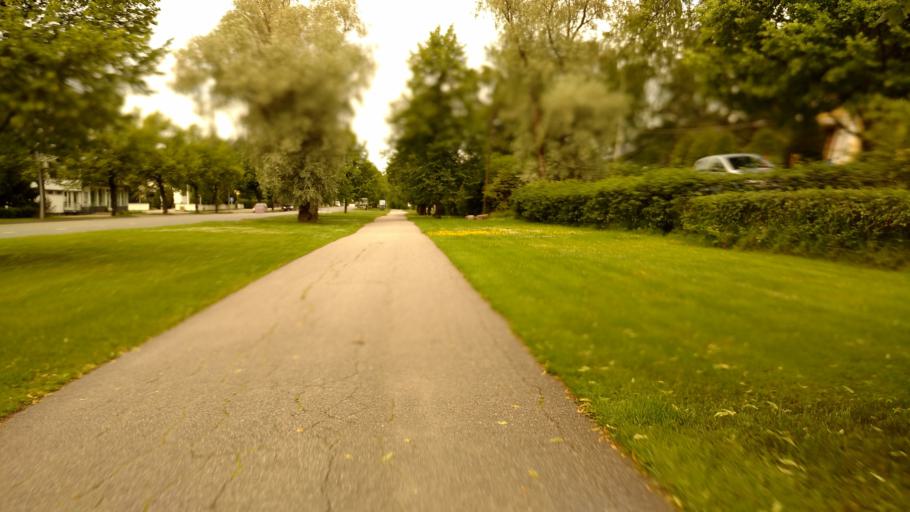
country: FI
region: Varsinais-Suomi
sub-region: Salo
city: Salo
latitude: 60.3784
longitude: 23.1361
